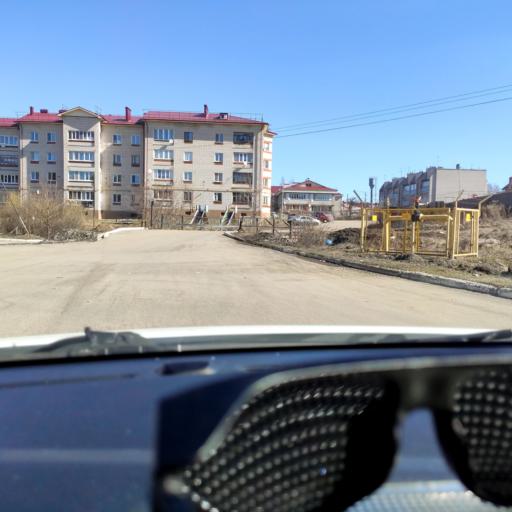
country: RU
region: Tatarstan
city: Vysokaya Gora
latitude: 55.9064
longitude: 49.2955
